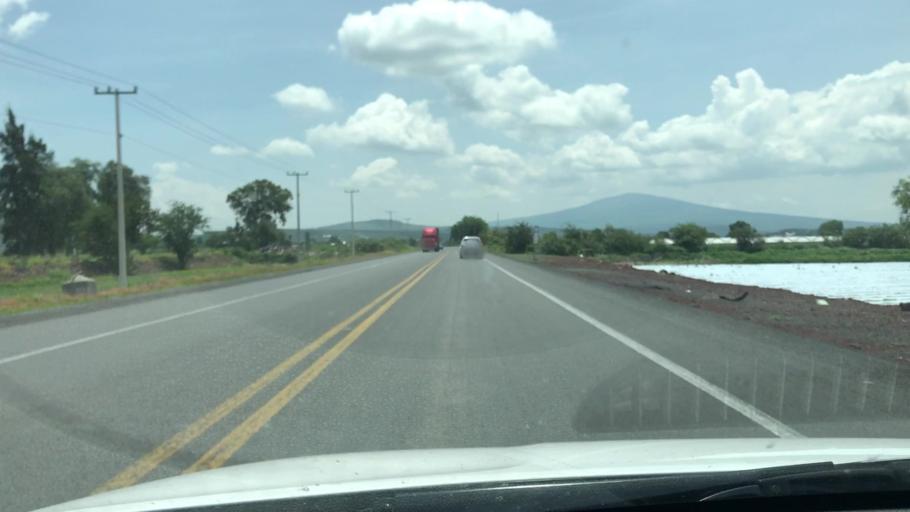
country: MX
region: Michoacan
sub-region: Yurecuaro
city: Yurecuaro
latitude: 20.3220
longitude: -102.2861
